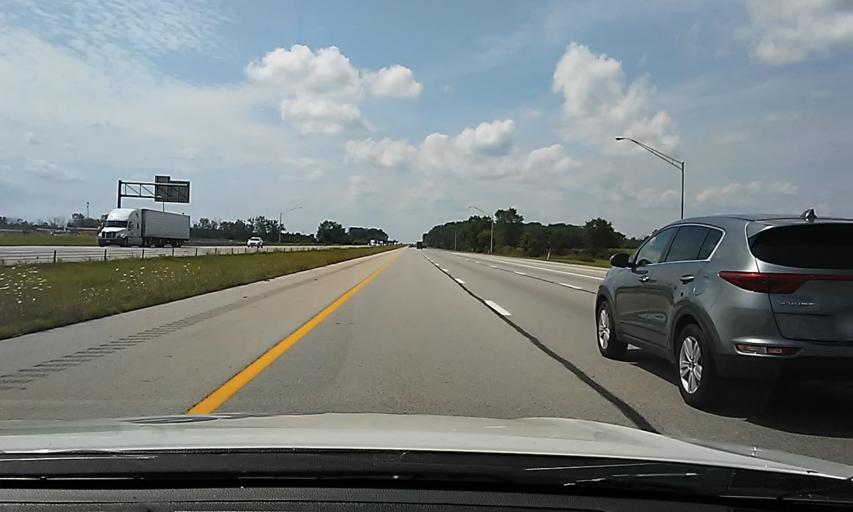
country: US
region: Ohio
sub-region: Clark County
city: Lisbon
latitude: 39.9331
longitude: -83.6146
